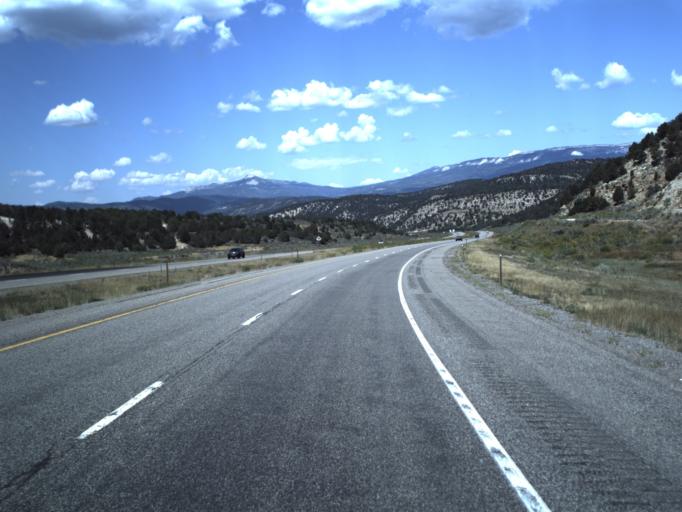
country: US
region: Utah
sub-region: Sevier County
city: Salina
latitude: 38.8242
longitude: -111.5394
